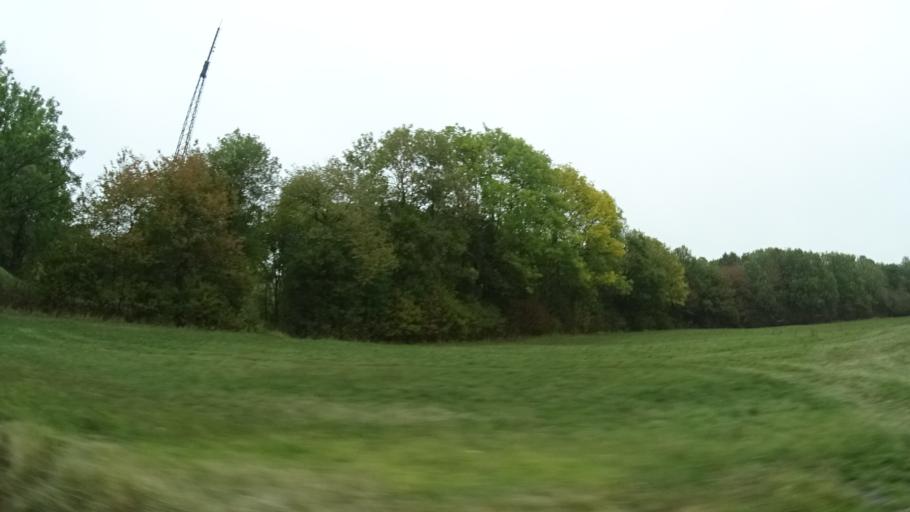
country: DE
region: Hesse
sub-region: Regierungsbezirk Kassel
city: Hilders
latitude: 50.5679
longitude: 10.0149
